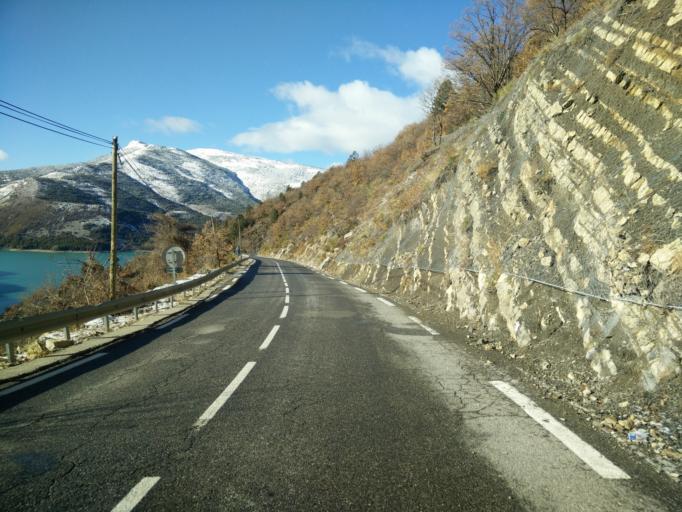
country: FR
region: Provence-Alpes-Cote d'Azur
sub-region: Departement des Alpes-de-Haute-Provence
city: Castellane
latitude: 43.9141
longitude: 6.5552
